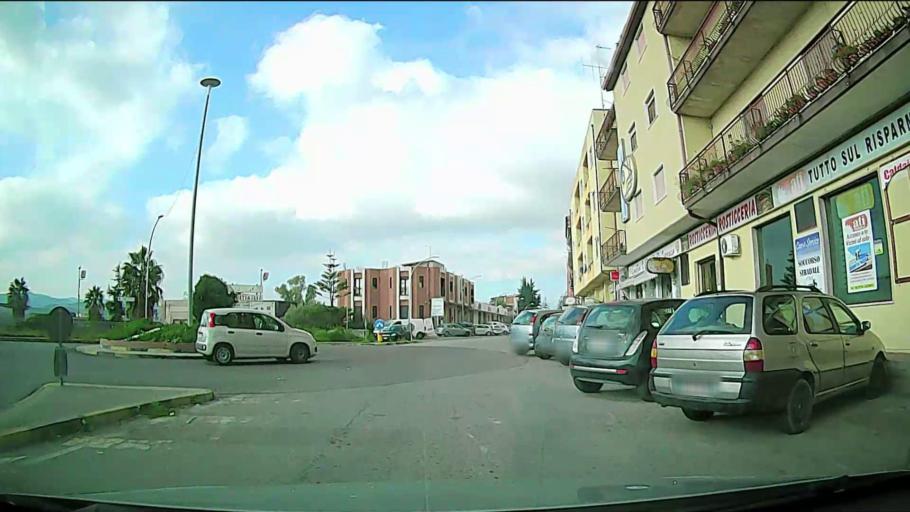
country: IT
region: Calabria
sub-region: Provincia di Crotone
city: Rocca di Neto
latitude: 39.1801
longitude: 17.0167
